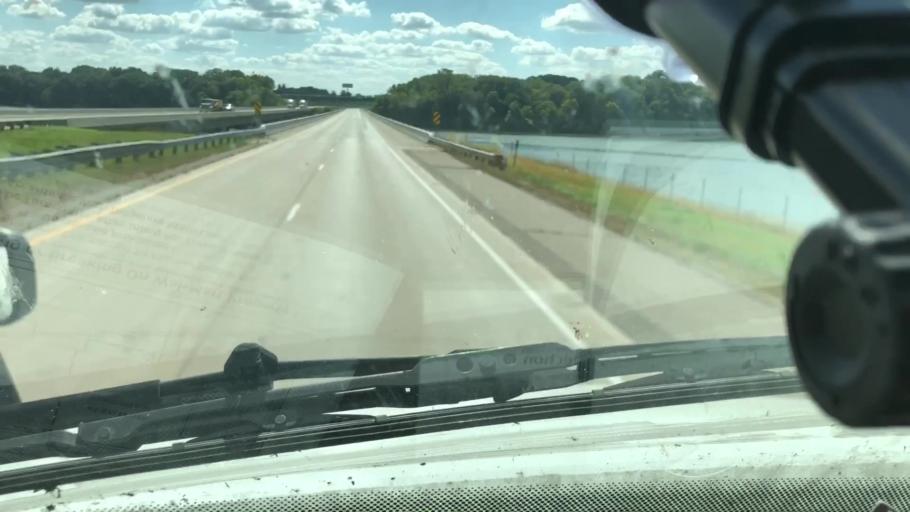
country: US
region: Minnesota
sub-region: Freeborn County
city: Albert Lea
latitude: 43.6300
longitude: -93.3276
